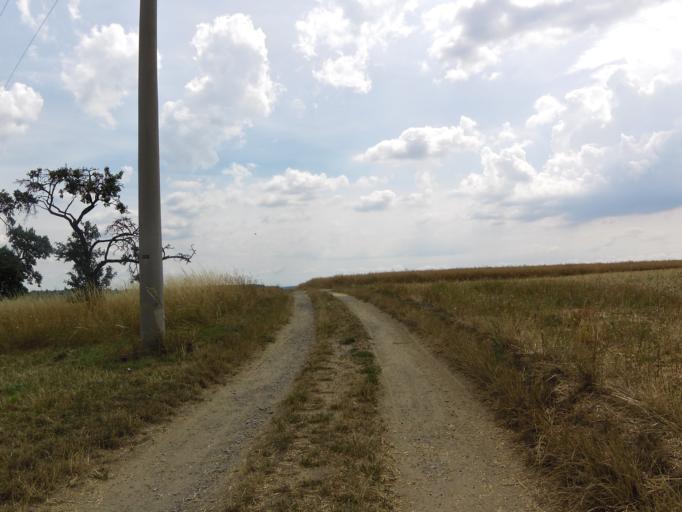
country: DE
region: Bavaria
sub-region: Regierungsbezirk Unterfranken
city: Gerbrunn
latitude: 49.7737
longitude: 9.9825
